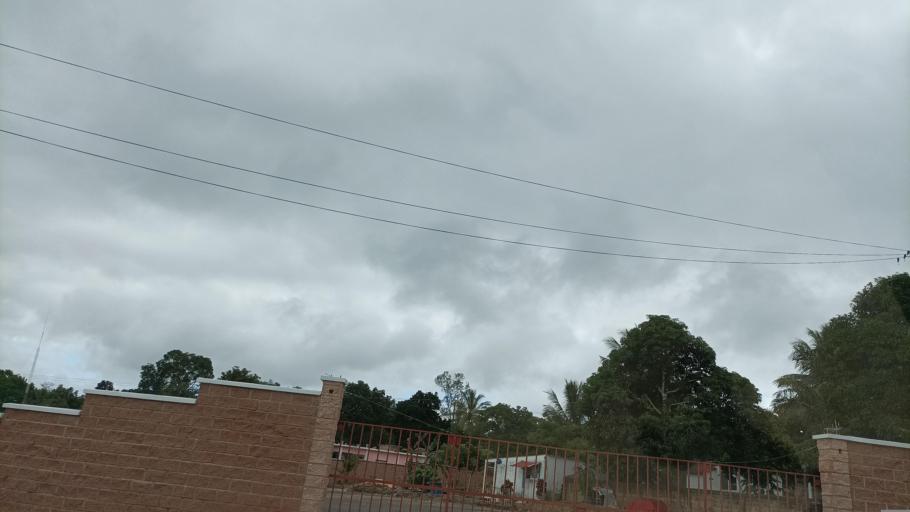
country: MX
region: Veracruz
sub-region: Cosoleacaque
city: Residencial las Olas
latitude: 18.0698
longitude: -94.5914
